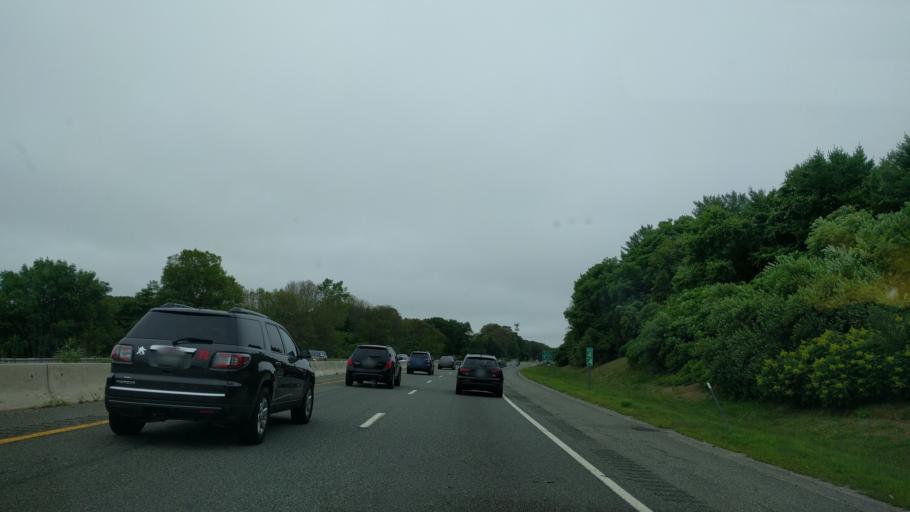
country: US
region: Rhode Island
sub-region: Washington County
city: Exeter
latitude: 41.5938
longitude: -71.4992
